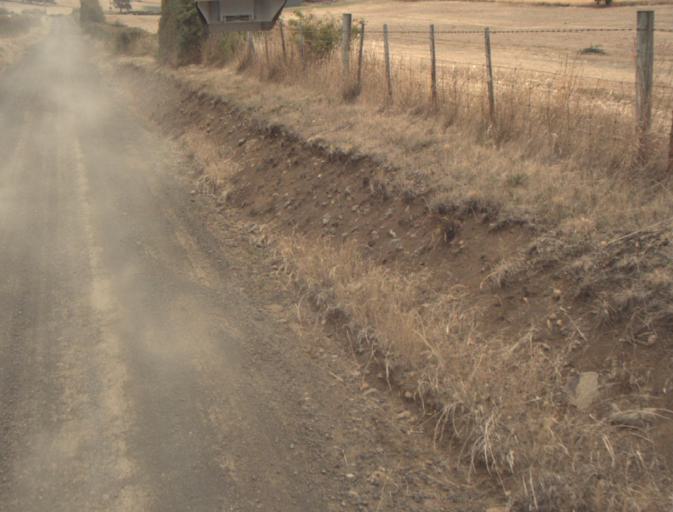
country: AU
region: Tasmania
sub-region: Northern Midlands
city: Evandale
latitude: -41.5198
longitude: 147.2616
